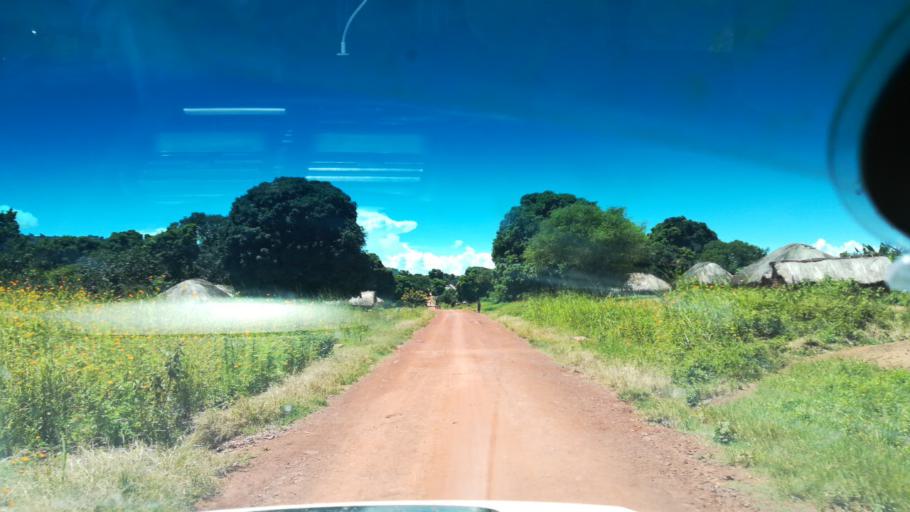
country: ZM
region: Luapula
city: Nchelenge
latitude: -8.7876
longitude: 28.6288
